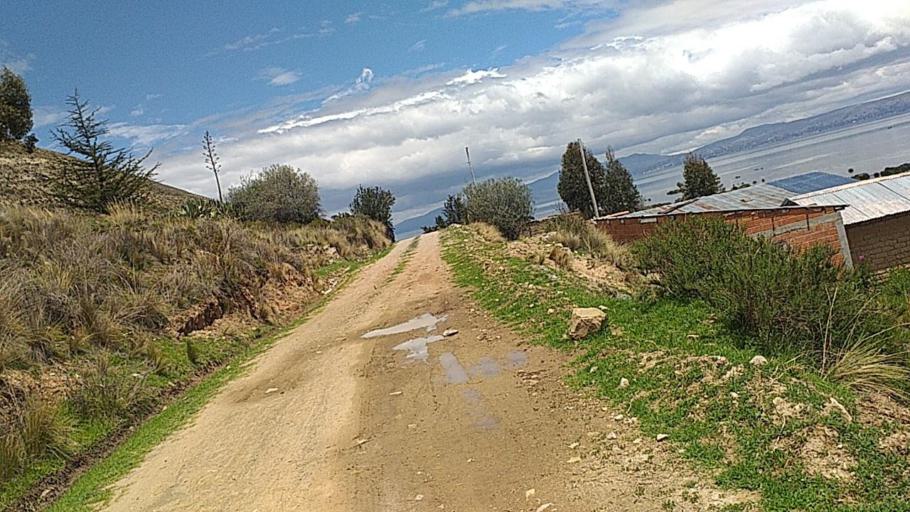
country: BO
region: La Paz
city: Huatajata
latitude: -16.3210
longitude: -68.6684
